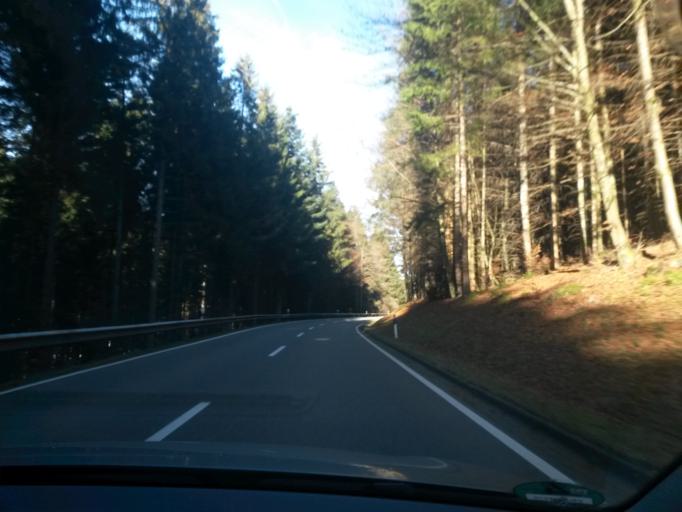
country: DE
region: Baden-Wuerttemberg
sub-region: Karlsruhe Region
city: Bad Wildbad
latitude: 48.7335
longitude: 8.5748
